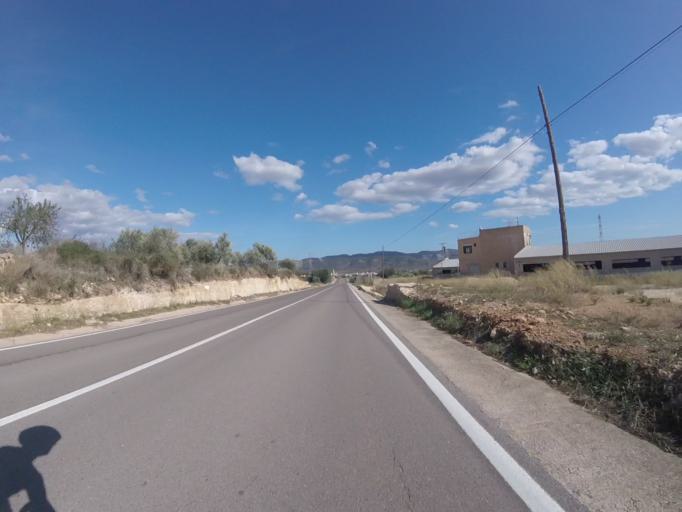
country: ES
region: Valencia
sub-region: Provincia de Castello
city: Alcala de Xivert
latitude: 40.3022
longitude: 0.1958
